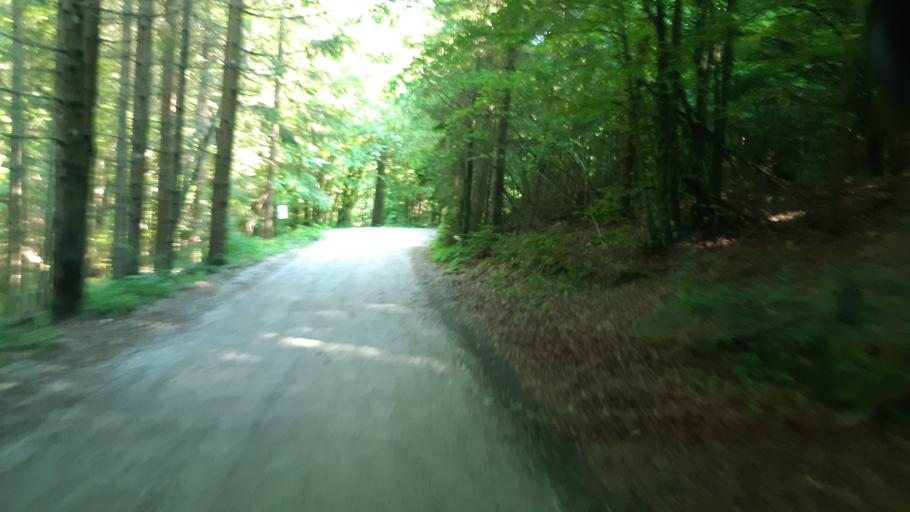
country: SI
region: Trzic
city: Bistrica pri Trzicu
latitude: 46.3689
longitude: 14.2775
